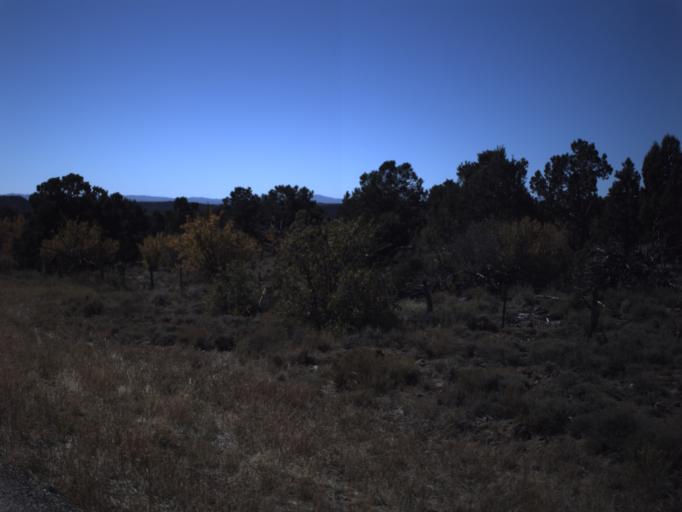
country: US
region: Utah
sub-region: Wayne County
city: Loa
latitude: 37.9805
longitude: -111.4308
